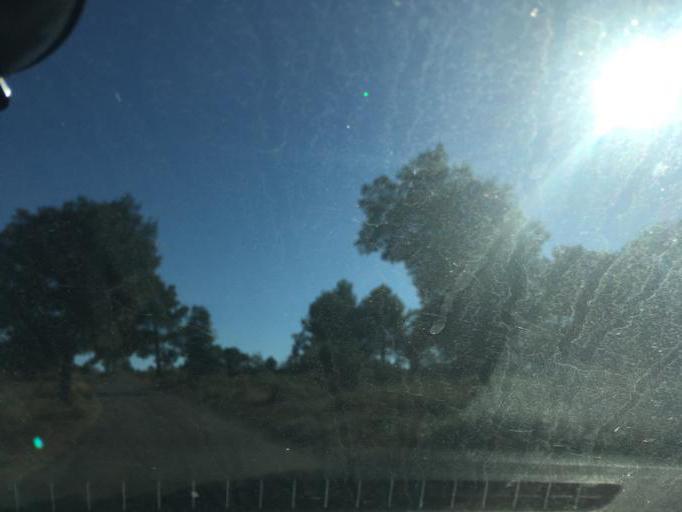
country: FR
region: Provence-Alpes-Cote d'Azur
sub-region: Departement des Alpes-de-Haute-Provence
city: Riez
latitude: 43.7402
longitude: 6.0985
